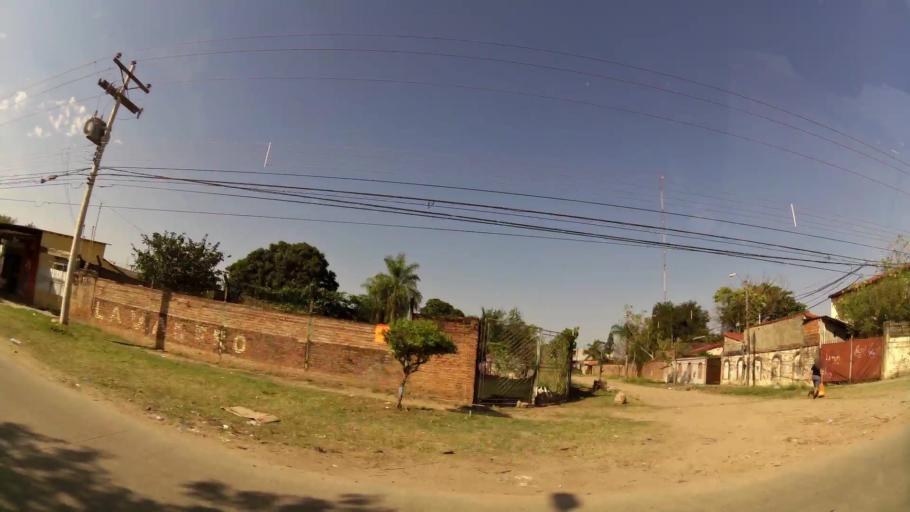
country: BO
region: Santa Cruz
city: Santa Cruz de la Sierra
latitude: -17.7988
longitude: -63.1423
